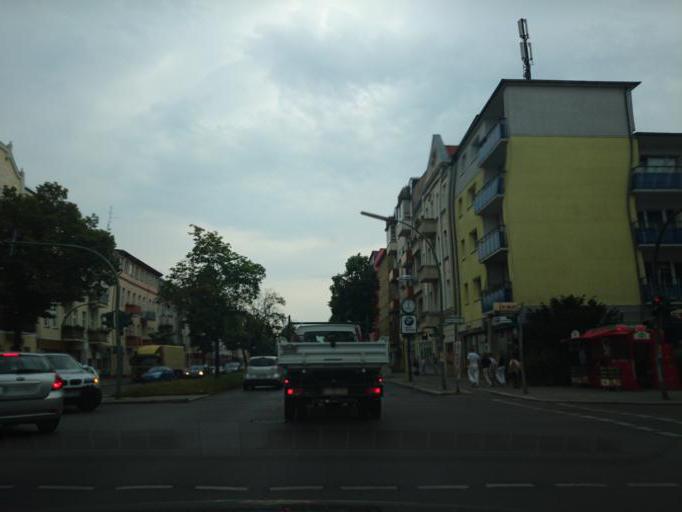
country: DE
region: Berlin
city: Lichterfelde
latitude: 52.4431
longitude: 13.3158
